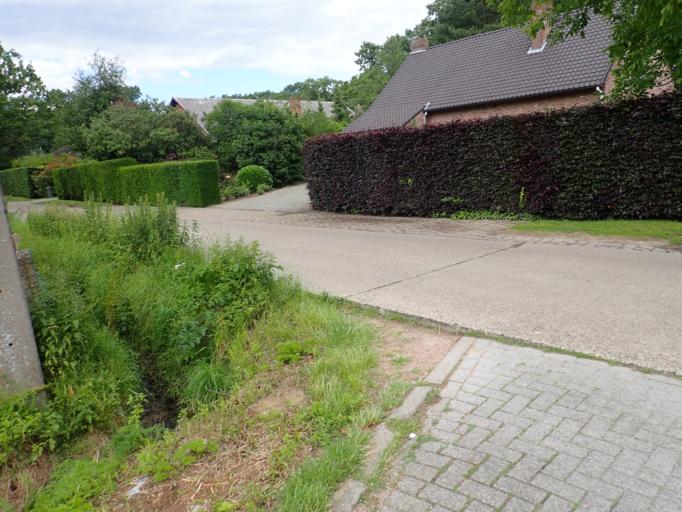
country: BE
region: Flanders
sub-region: Provincie Antwerpen
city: Heist-op-den-Berg
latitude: 51.0990
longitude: 4.7104
